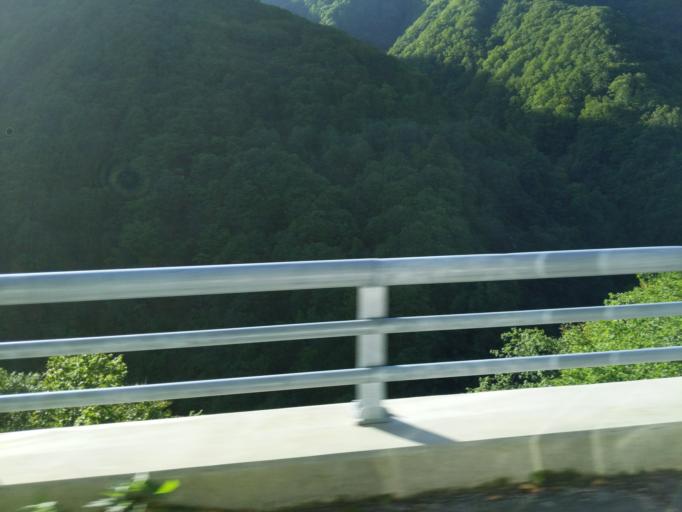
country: JP
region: Toyama
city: Kamiichi
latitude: 36.5096
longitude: 137.4492
